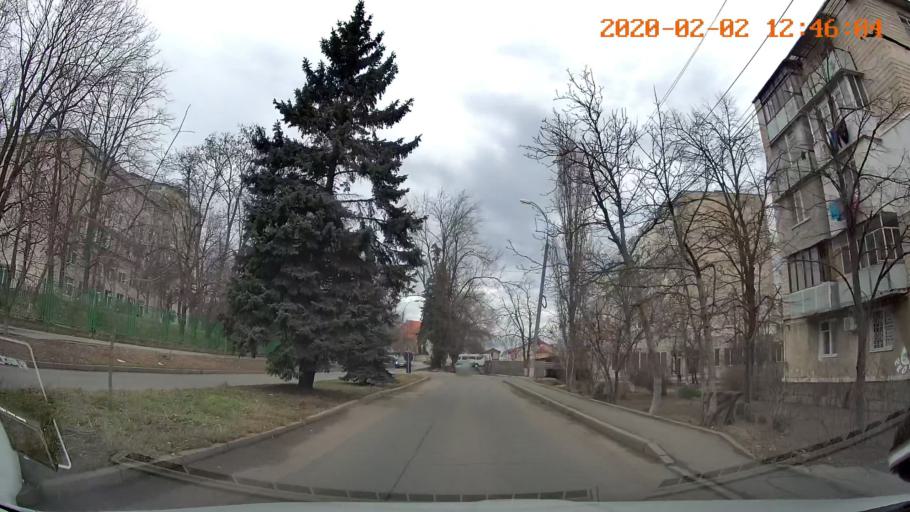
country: MD
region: Chisinau
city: Chisinau
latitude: 47.0076
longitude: 28.8167
